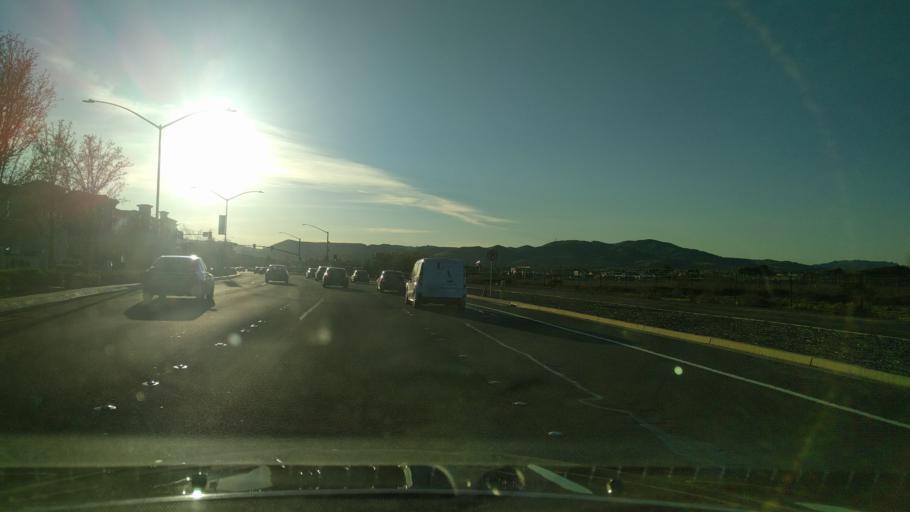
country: US
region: California
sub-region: Alameda County
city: Dublin
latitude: 37.7065
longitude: -121.8955
